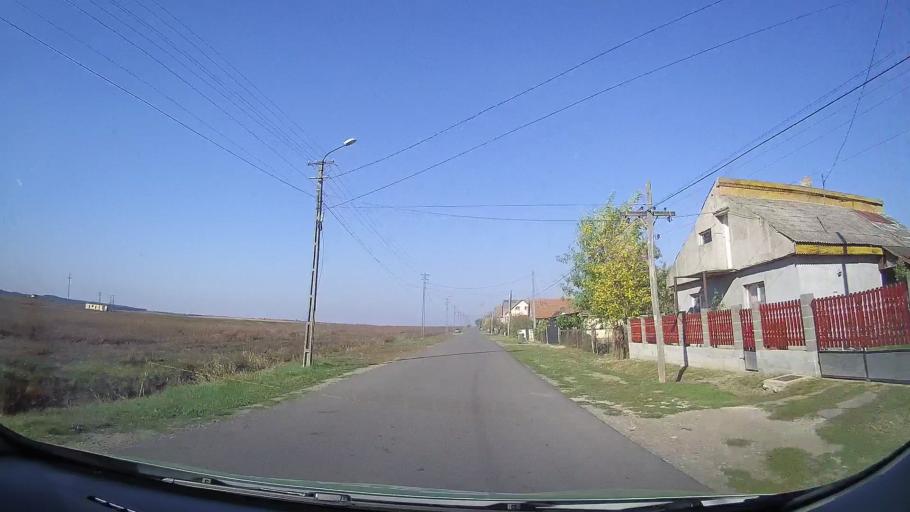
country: RO
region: Satu Mare
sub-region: Oras Tasnad
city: Tasnad
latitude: 47.4759
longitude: 22.5628
